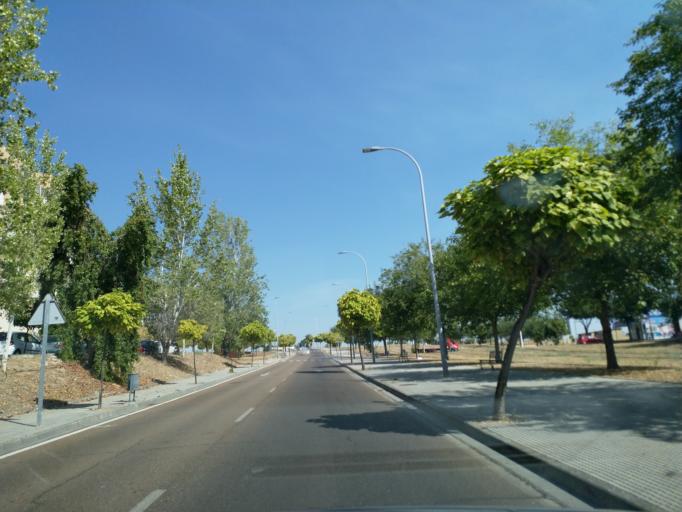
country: ES
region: Extremadura
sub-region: Provincia de Badajoz
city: Merida
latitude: 38.9335
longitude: -6.3462
